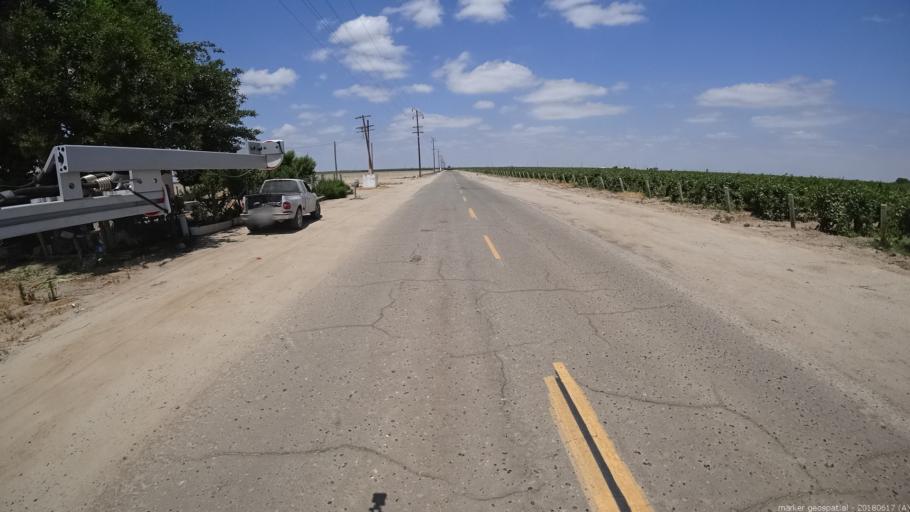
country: US
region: California
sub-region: Fresno County
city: Biola
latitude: 36.8304
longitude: -120.1150
